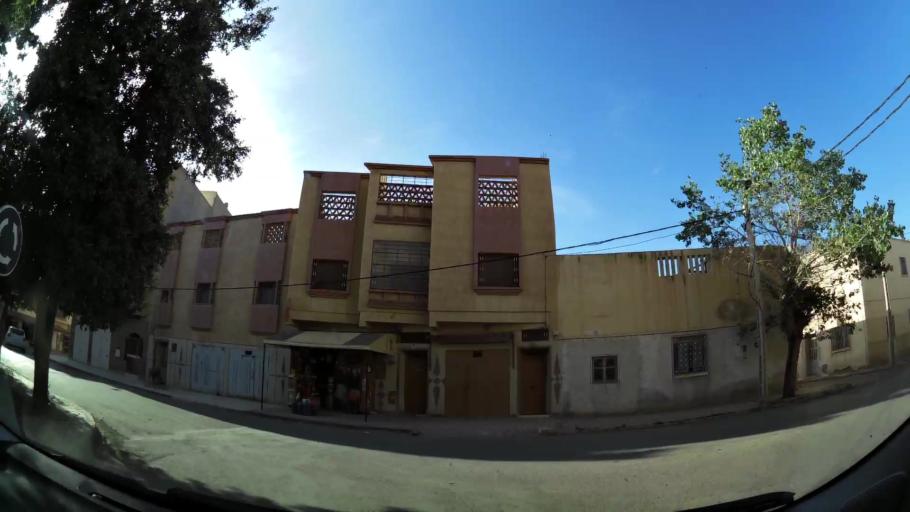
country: MA
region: Oriental
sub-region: Oujda-Angad
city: Oujda
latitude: 34.6947
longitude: -1.9156
